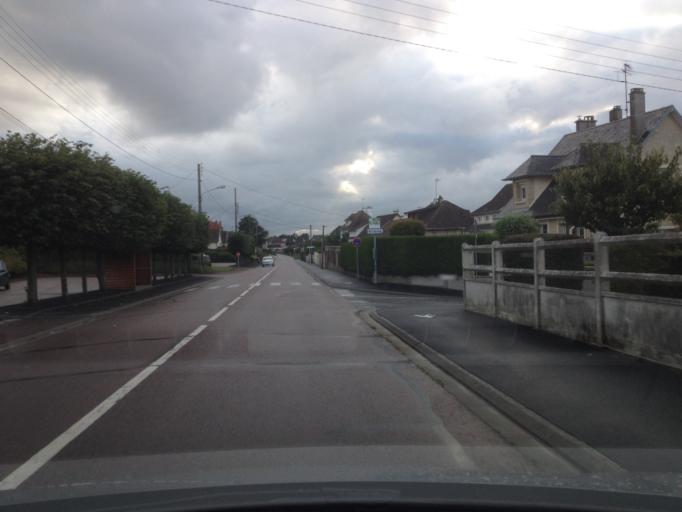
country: FR
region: Lower Normandy
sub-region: Departement du Calvados
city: Grandcamp-Maisy
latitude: 49.3867
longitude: -1.0447
